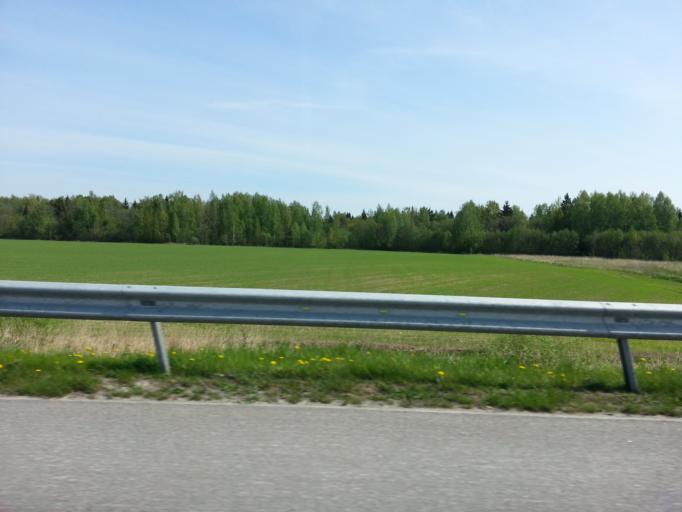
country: LT
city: Ramygala
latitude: 55.5374
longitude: 24.5418
